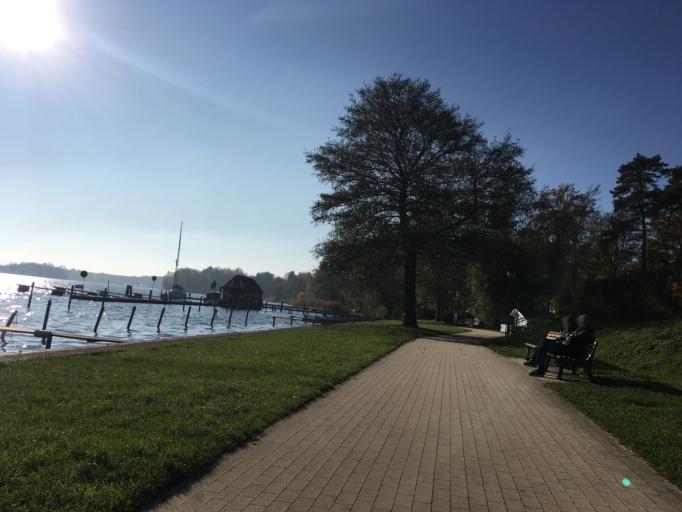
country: DE
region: Brandenburg
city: Bad Saarow
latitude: 52.2909
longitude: 14.0469
